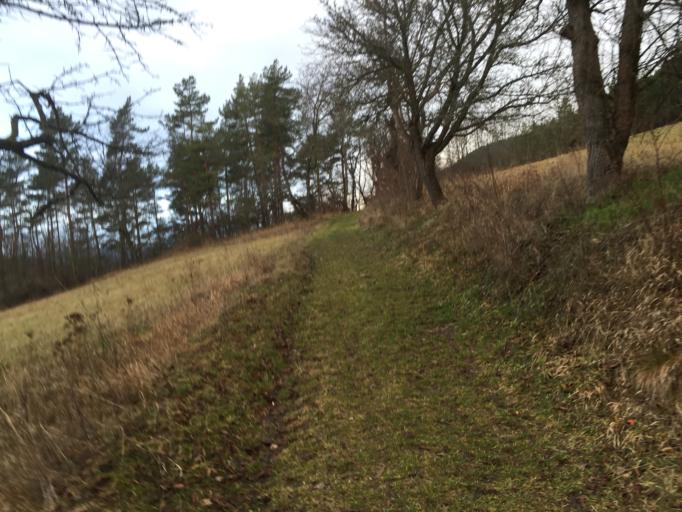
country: DE
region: Thuringia
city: Bad Blankenburg
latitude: 50.6979
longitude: 11.2559
